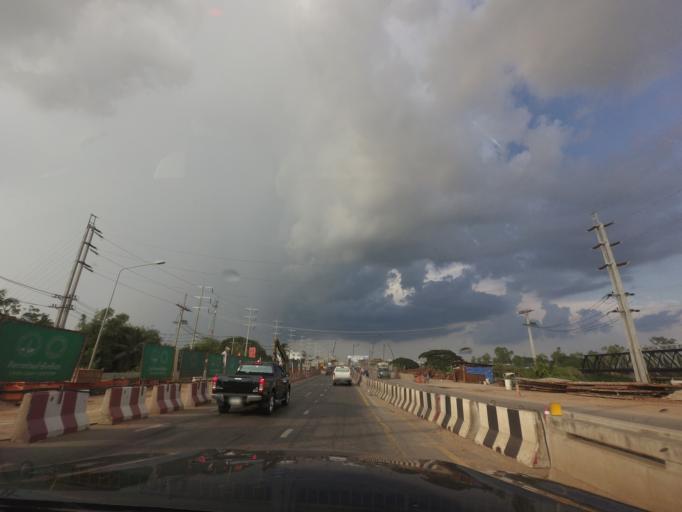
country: TH
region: Khon Kaen
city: Khon Kaen
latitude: 16.3709
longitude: 102.8086
